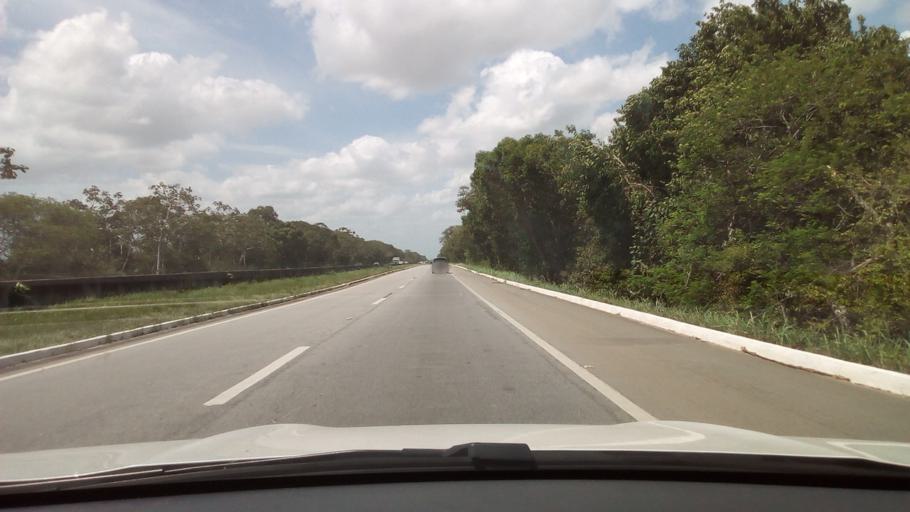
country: BR
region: Paraiba
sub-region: Mamanguape
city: Mamanguape
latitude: -6.9020
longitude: -35.1197
